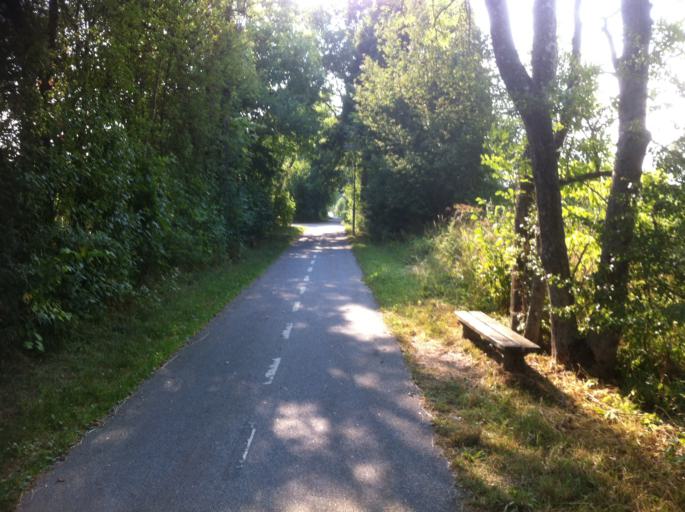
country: SE
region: Skane
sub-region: Lunds Kommun
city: Genarp
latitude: 55.7127
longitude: 13.3251
